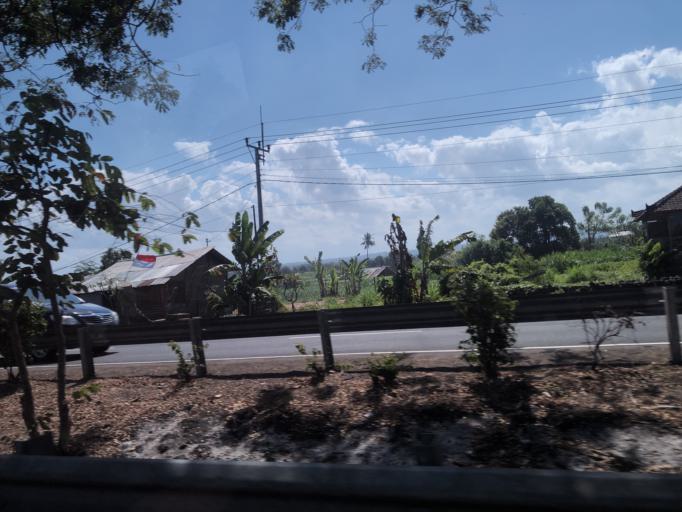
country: ID
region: Bali
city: Semarapura
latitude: -8.5687
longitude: 115.4091
